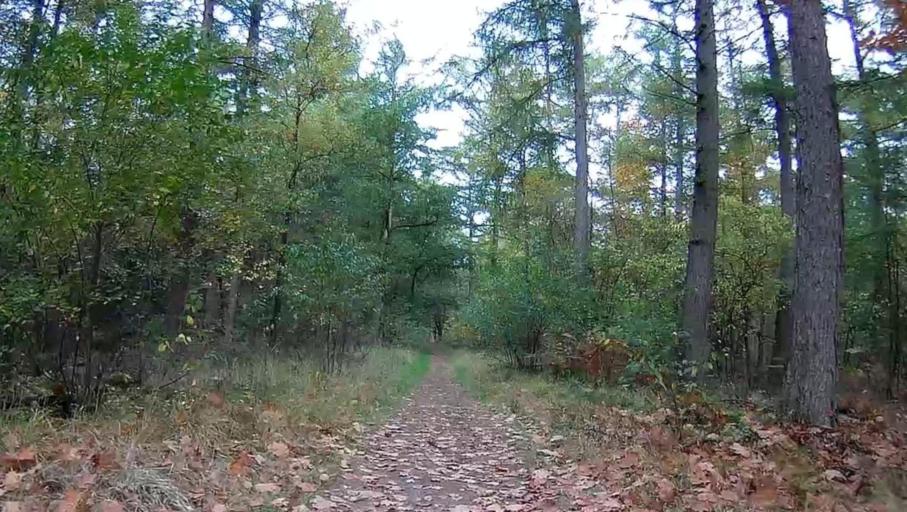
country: NL
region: Gelderland
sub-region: Gemeente Ede
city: Ede
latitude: 52.0668
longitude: 5.6790
